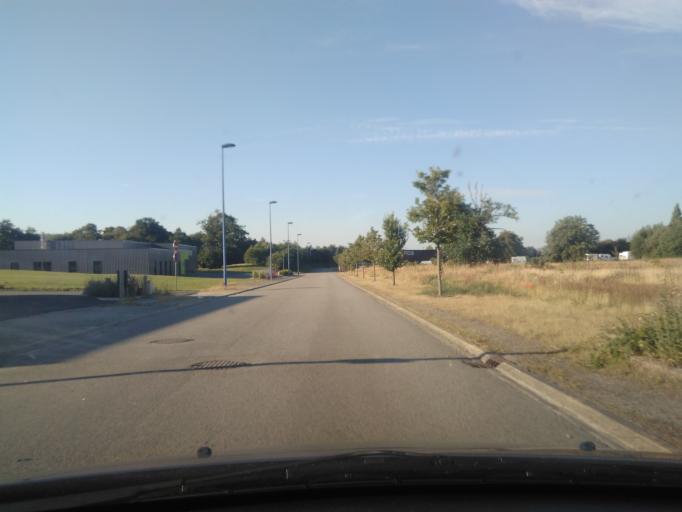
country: FR
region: Pays de la Loire
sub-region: Departement de la Vendee
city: Mouilleron-le-Captif
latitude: 46.7409
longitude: -1.4267
